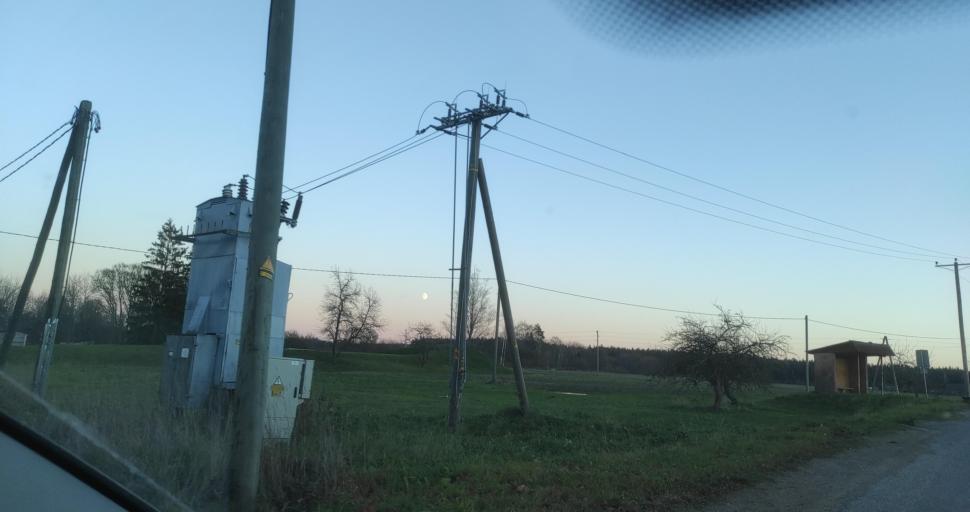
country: LV
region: Dundaga
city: Dundaga
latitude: 57.3752
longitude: 22.2301
